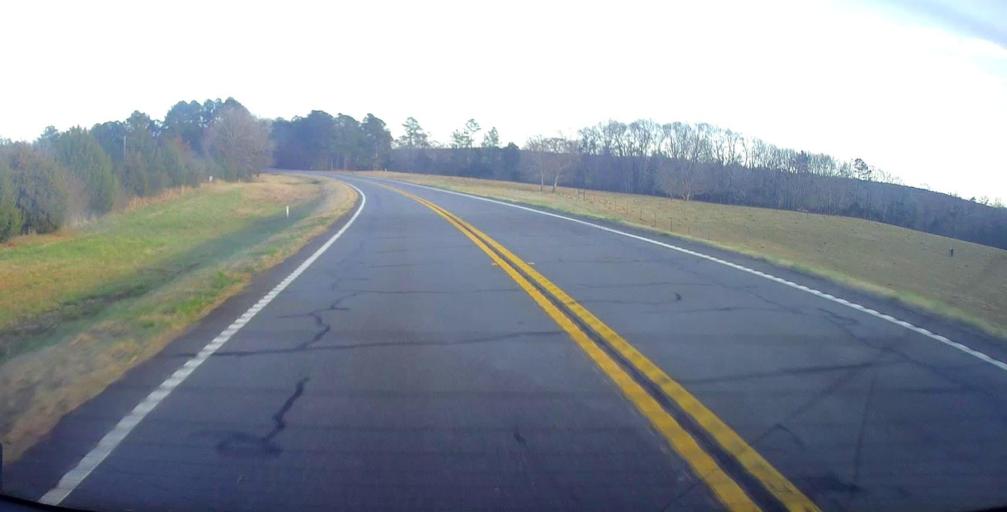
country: US
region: Georgia
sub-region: Talbot County
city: Talbotton
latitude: 32.7852
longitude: -84.5278
